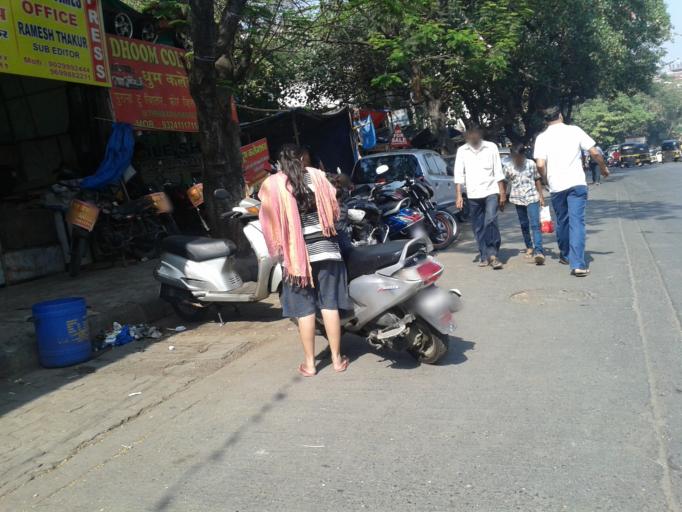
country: IN
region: Maharashtra
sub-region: Mumbai Suburban
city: Borivli
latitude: 19.2512
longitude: 72.8637
